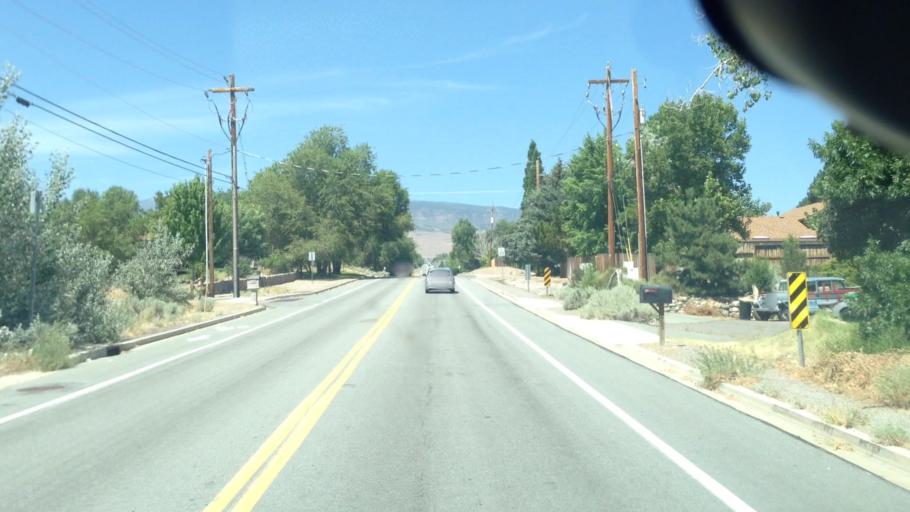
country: US
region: Nevada
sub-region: Washoe County
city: Sparks
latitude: 39.4187
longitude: -119.7660
